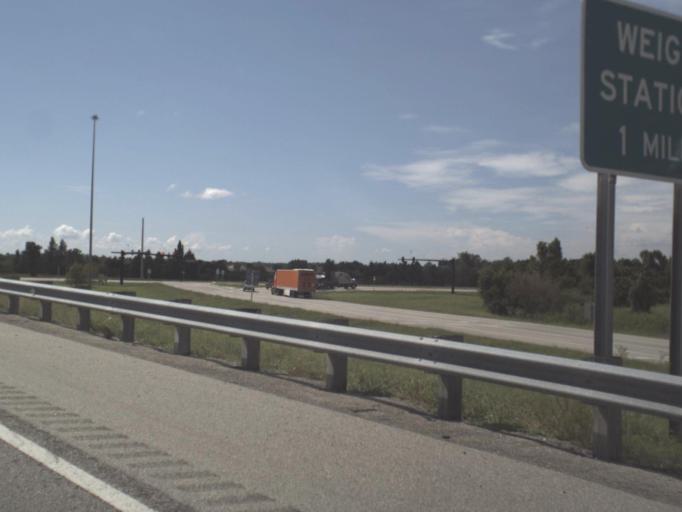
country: US
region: Florida
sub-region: Charlotte County
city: Charlotte Park
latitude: 26.8970
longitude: -82.0046
